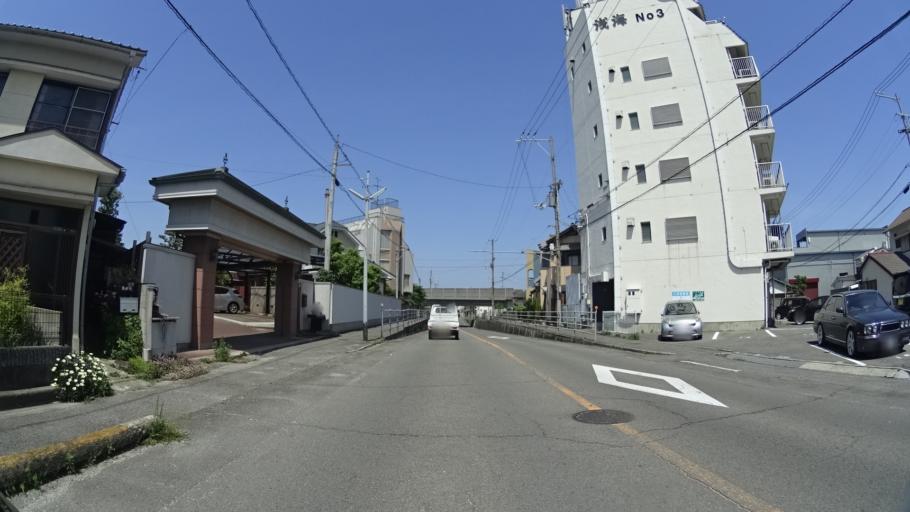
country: JP
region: Ehime
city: Saijo
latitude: 34.0559
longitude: 132.9982
